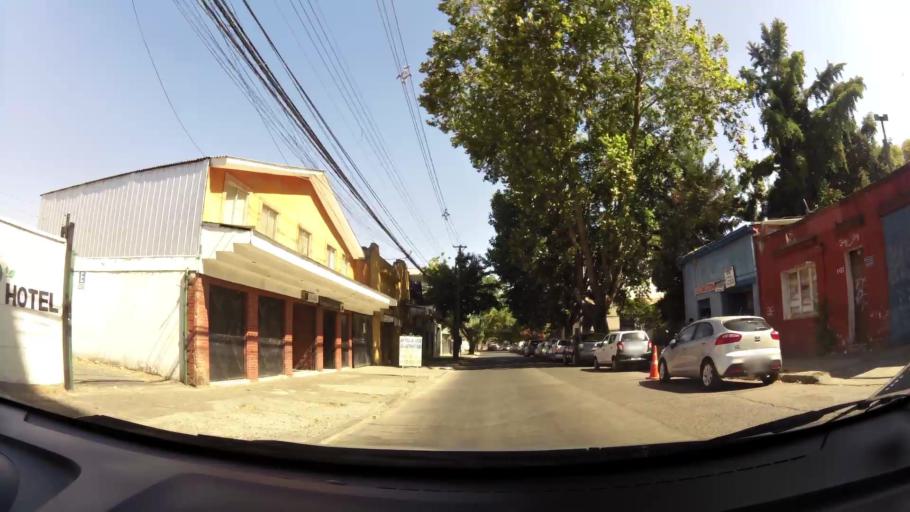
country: CL
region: Maule
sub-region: Provincia de Talca
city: Talca
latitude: -35.4231
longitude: -71.6595
